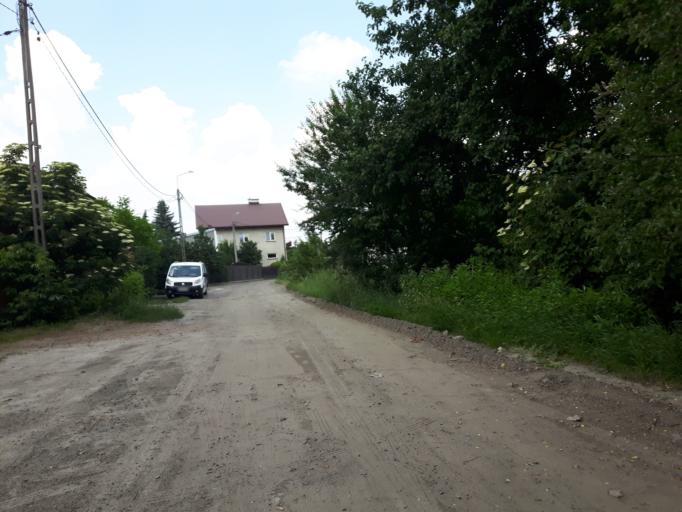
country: PL
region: Masovian Voivodeship
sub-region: Powiat wolominski
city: Zabki
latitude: 52.2829
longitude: 21.1166
